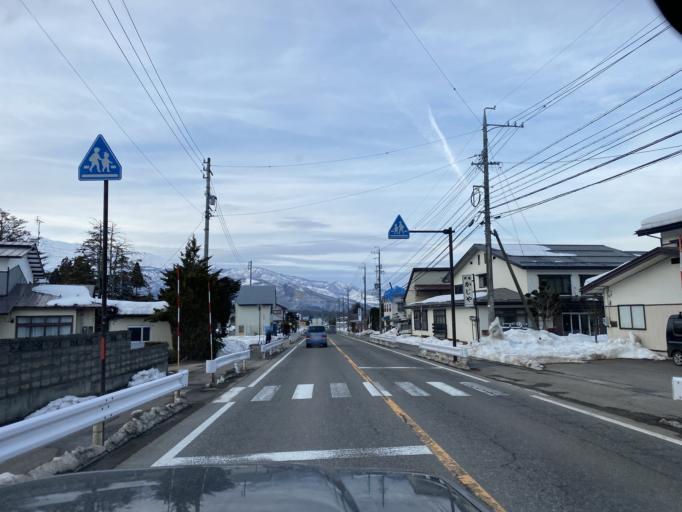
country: JP
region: Nagano
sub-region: Kitaazumi Gun
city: Hakuba
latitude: 36.6621
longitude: 137.8489
